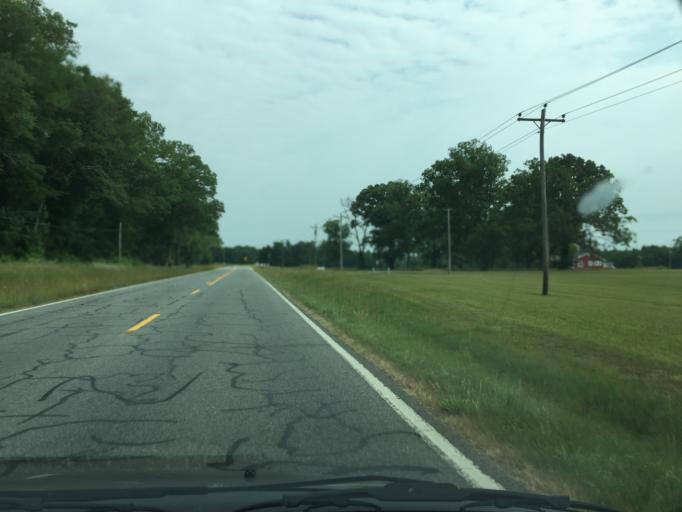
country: US
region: Georgia
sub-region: Catoosa County
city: Ringgold
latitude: 34.8513
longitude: -85.1425
